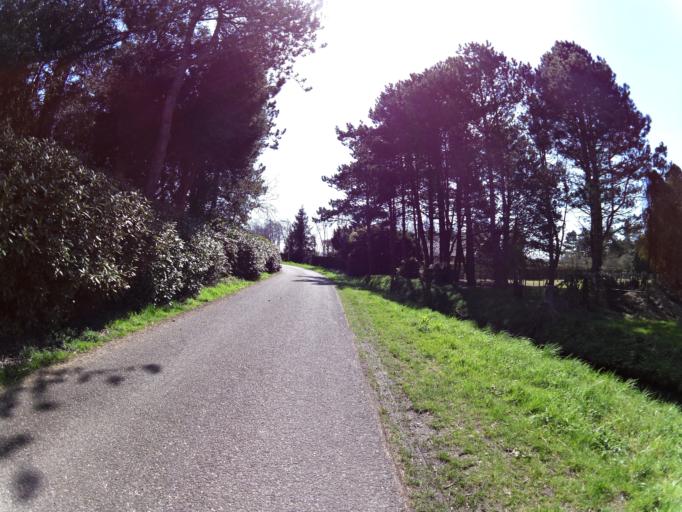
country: NL
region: South Holland
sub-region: Gemeente Hellevoetsluis
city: Nieuw-Helvoet
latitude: 51.8959
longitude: 4.0792
